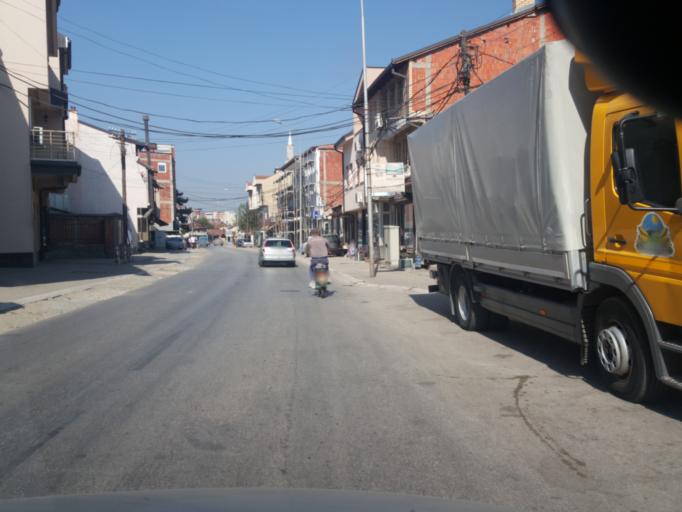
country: XK
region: Gjakova
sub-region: Komuna e Gjakoves
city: Gjakove
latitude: 42.3738
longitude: 20.4245
